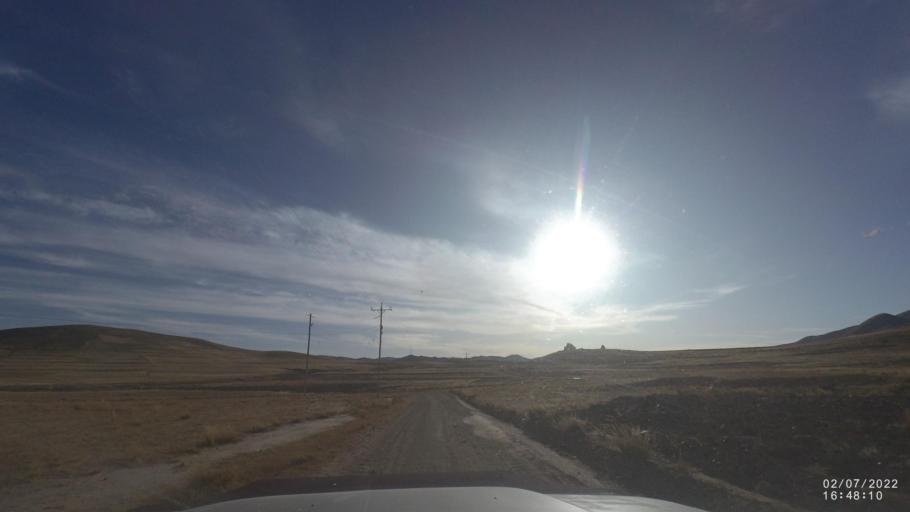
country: BO
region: Cochabamba
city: Irpa Irpa
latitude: -17.9786
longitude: -66.5173
